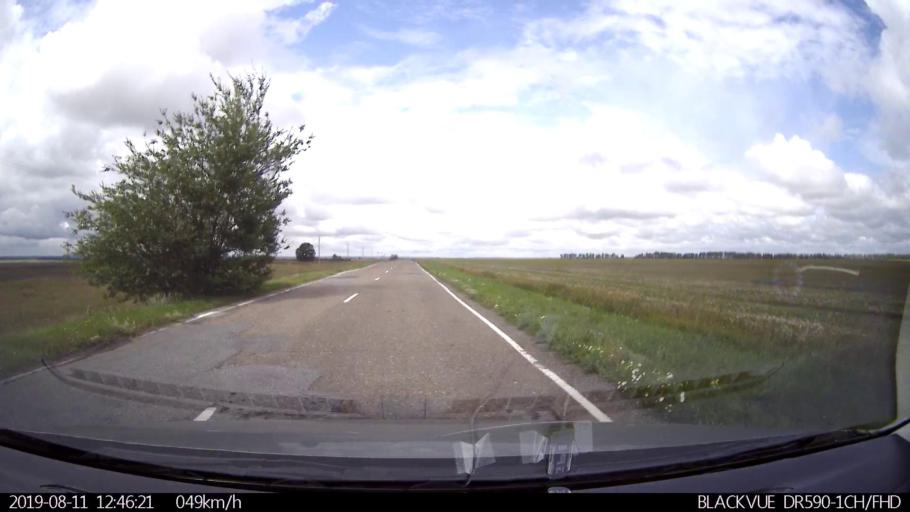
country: RU
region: Ulyanovsk
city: Ignatovka
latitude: 53.8638
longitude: 47.7196
